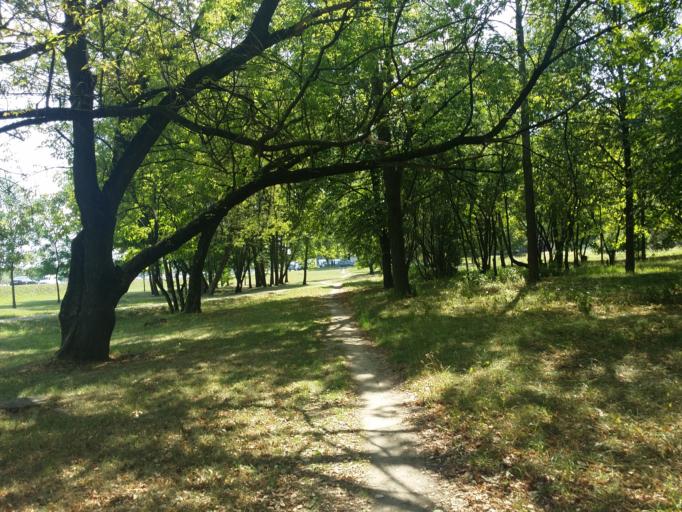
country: BY
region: Minsk
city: Vyaliki Trastsyanets
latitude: 53.8558
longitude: 27.6888
